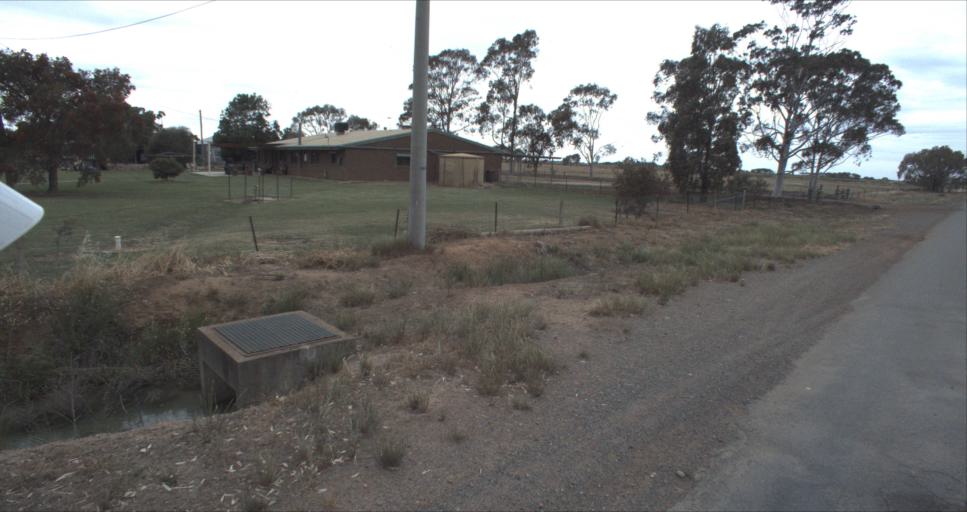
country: AU
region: New South Wales
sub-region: Leeton
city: Leeton
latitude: -34.4206
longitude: 146.3386
